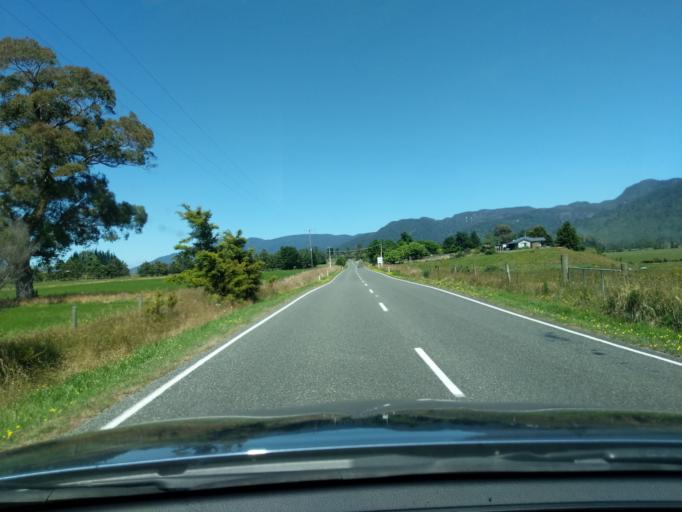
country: NZ
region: Tasman
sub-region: Tasman District
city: Takaka
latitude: -40.6841
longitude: 172.6604
